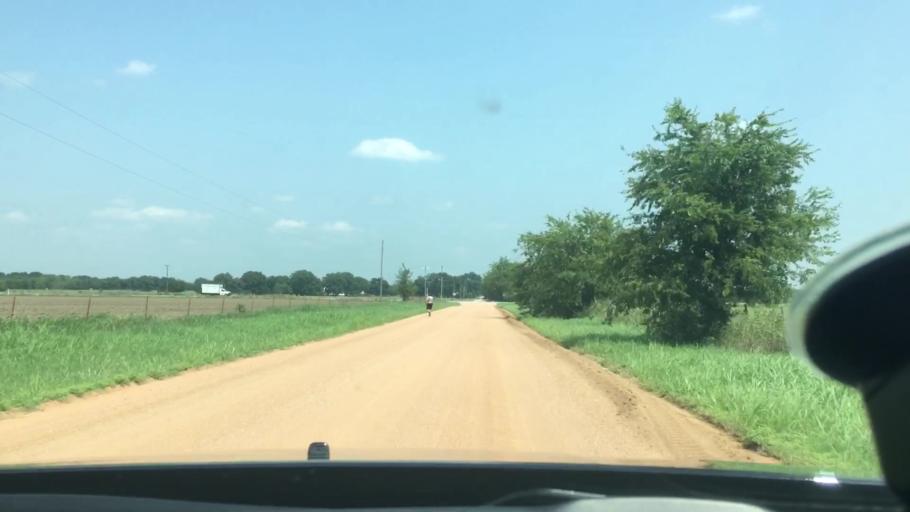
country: US
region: Oklahoma
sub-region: Coal County
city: Coalgate
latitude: 34.4330
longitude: -96.4272
